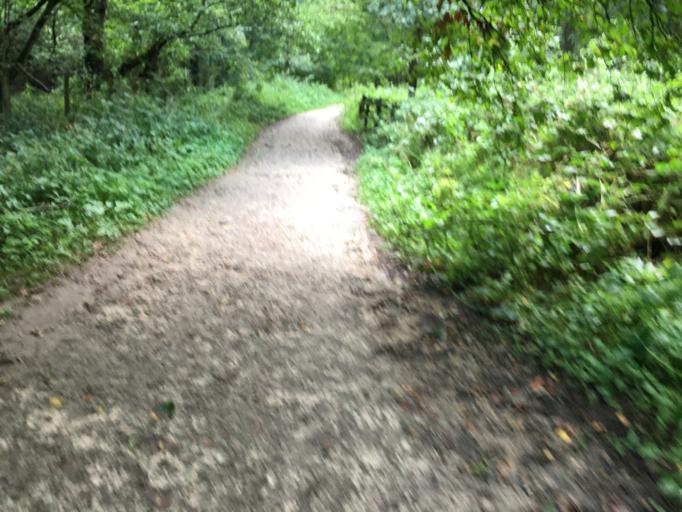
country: GB
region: England
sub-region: North Yorkshire
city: Sleights
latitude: 54.4061
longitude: -0.7311
